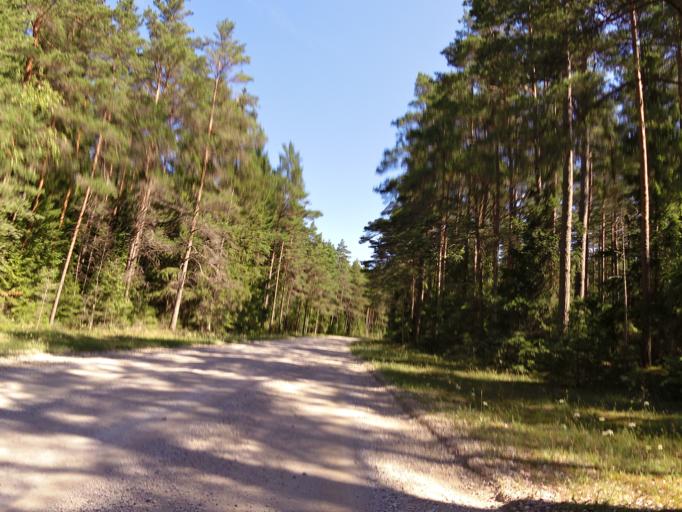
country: EE
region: Hiiumaa
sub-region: Kaerdla linn
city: Kardla
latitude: 58.9179
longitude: 22.3456
